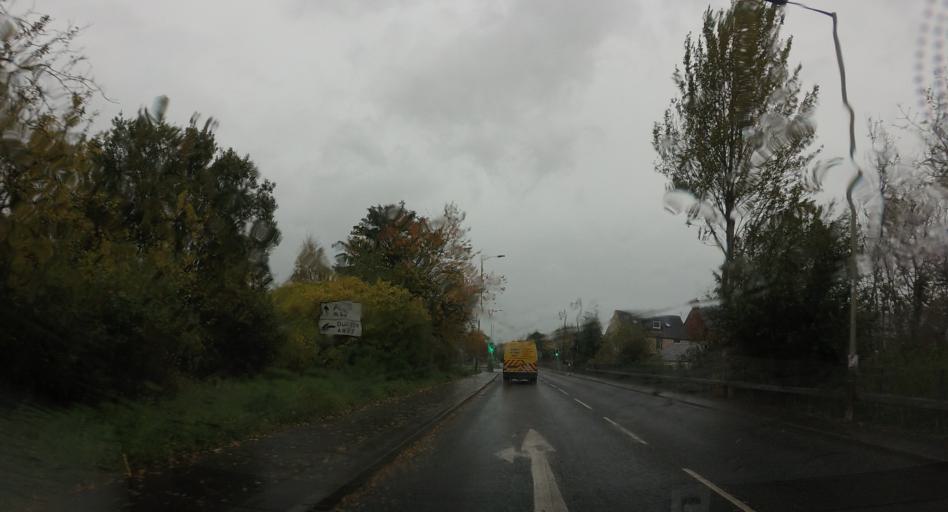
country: GB
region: Scotland
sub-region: Perth and Kinross
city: Coupar Angus
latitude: 56.5454
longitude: -3.2660
